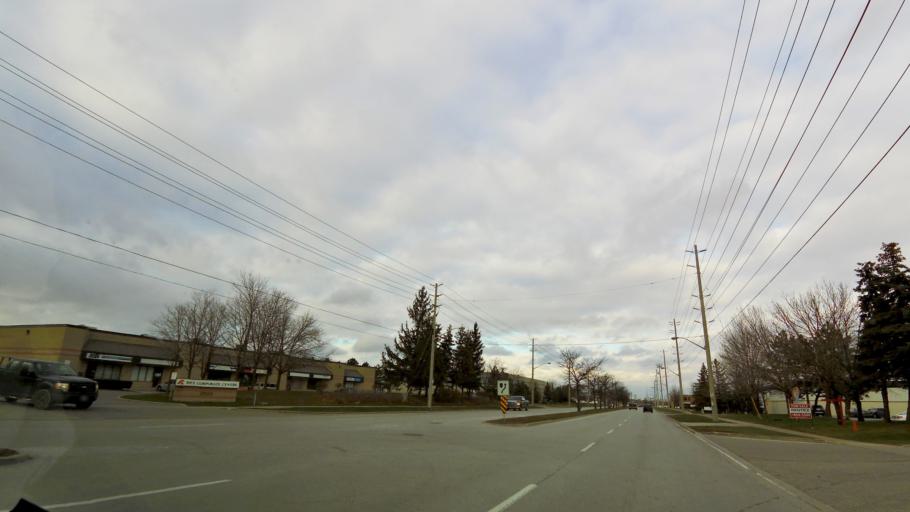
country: CA
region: Ontario
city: Brampton
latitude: 43.7588
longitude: -79.7025
